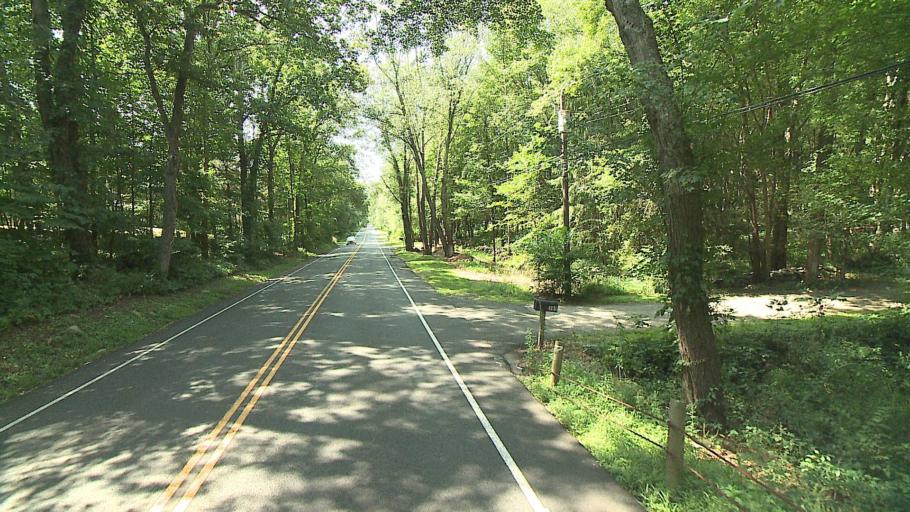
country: US
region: Connecticut
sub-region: Fairfield County
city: Trumbull
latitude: 41.2962
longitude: -73.2877
